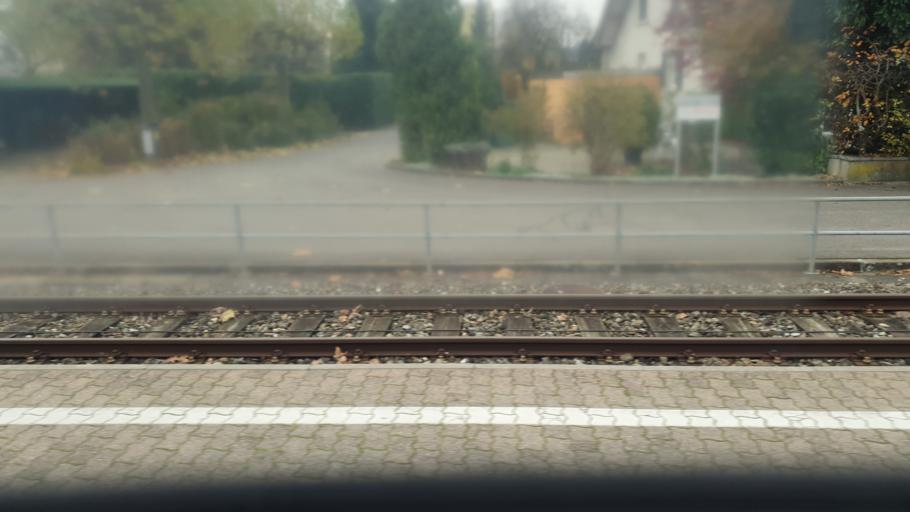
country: CH
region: Aargau
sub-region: Bezirk Aarau
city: Oberentfelden
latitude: 47.3611
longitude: 8.0456
